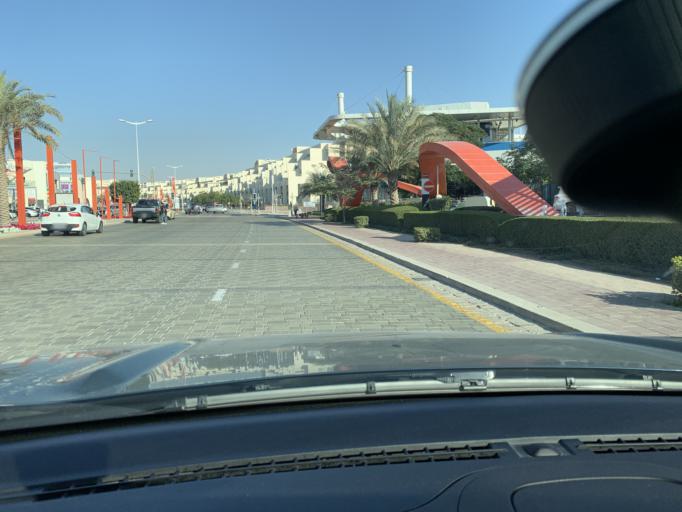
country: AE
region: Dubai
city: Dubai
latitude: 25.0461
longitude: 55.2397
